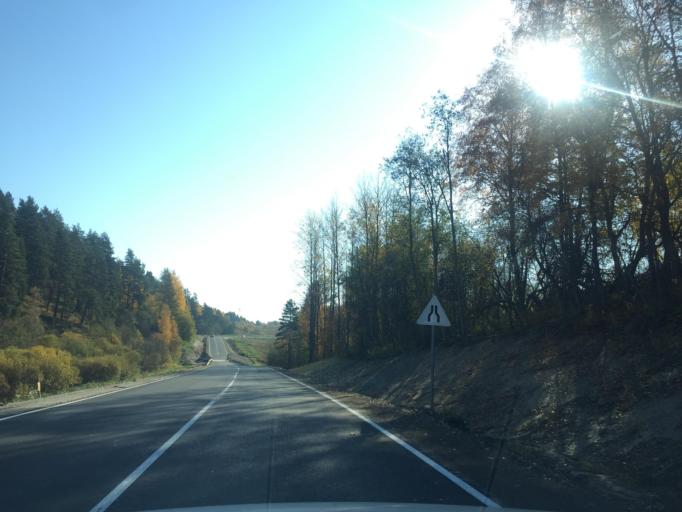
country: RU
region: Leningrad
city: Kuznechnoye
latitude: 61.3177
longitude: 29.8709
